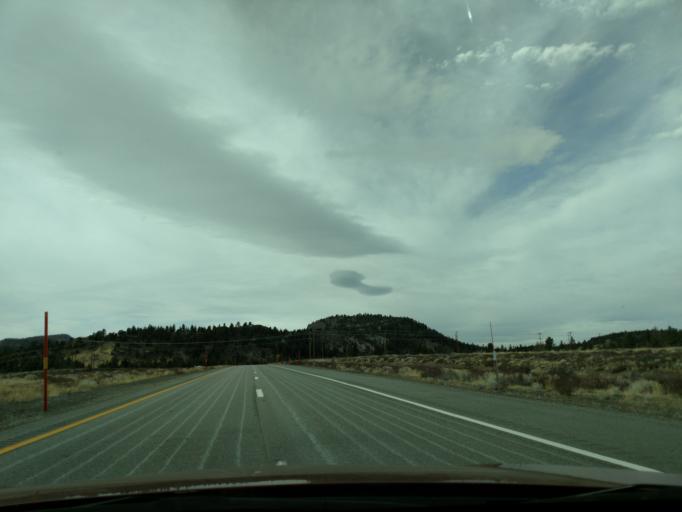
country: US
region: California
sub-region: Mono County
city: Mammoth Lakes
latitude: 37.6417
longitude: -118.9171
